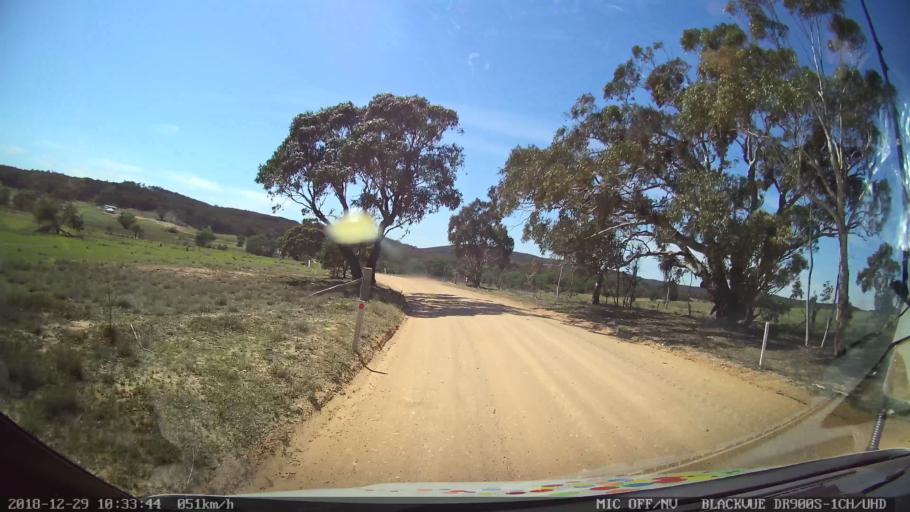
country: AU
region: New South Wales
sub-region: Yass Valley
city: Gundaroo
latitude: -34.9828
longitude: 149.4734
